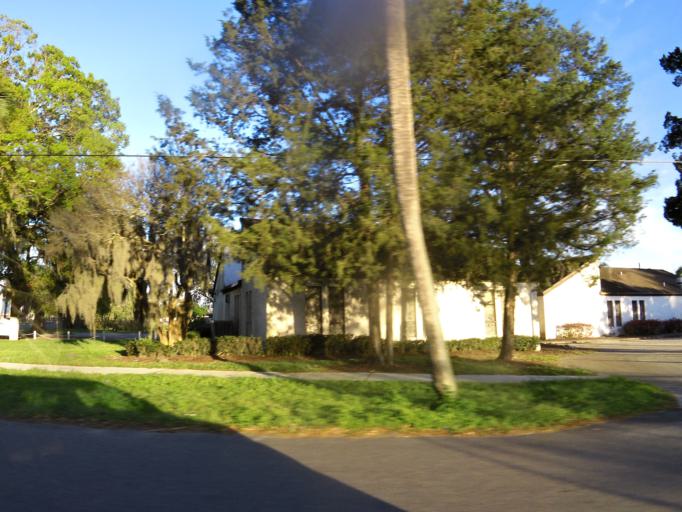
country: US
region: Florida
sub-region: Duval County
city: Jacksonville
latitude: 30.3401
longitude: -81.7088
